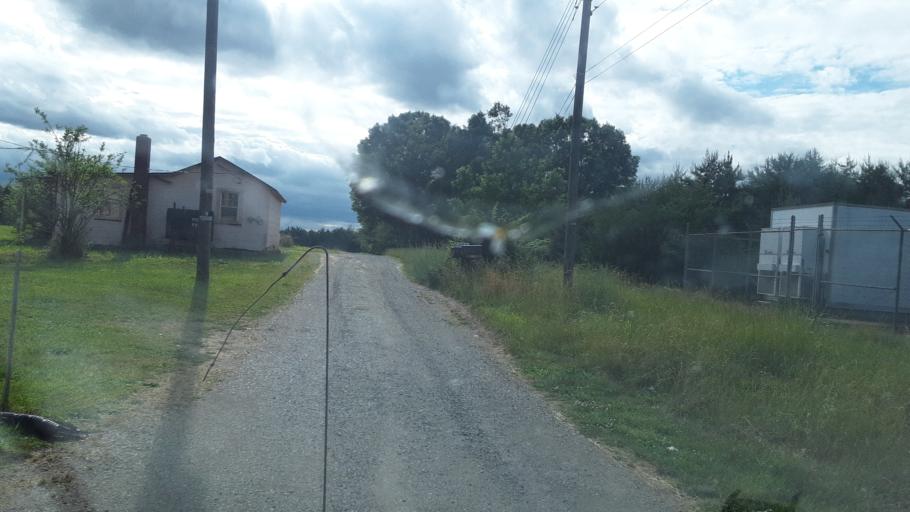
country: US
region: Virginia
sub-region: Pittsylvania County
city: Chatham
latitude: 36.8459
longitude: -79.3970
